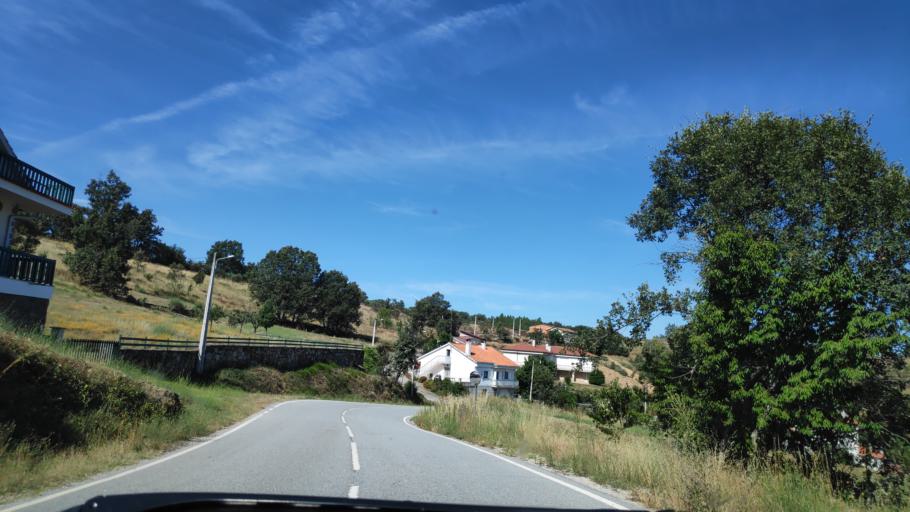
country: ES
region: Castille and Leon
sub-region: Provincia de Zamora
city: Alcanices
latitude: 41.6298
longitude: -6.3511
